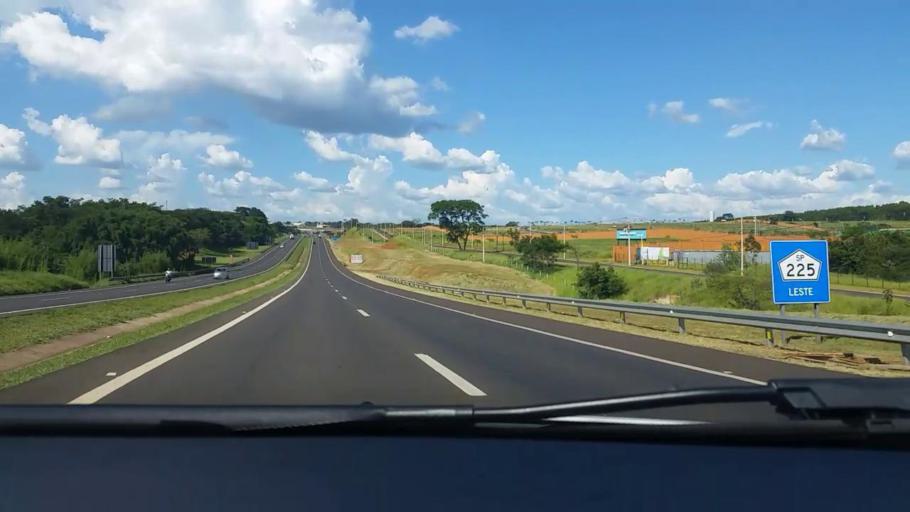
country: BR
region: Sao Paulo
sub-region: Bauru
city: Bauru
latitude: -22.3732
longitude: -49.0550
